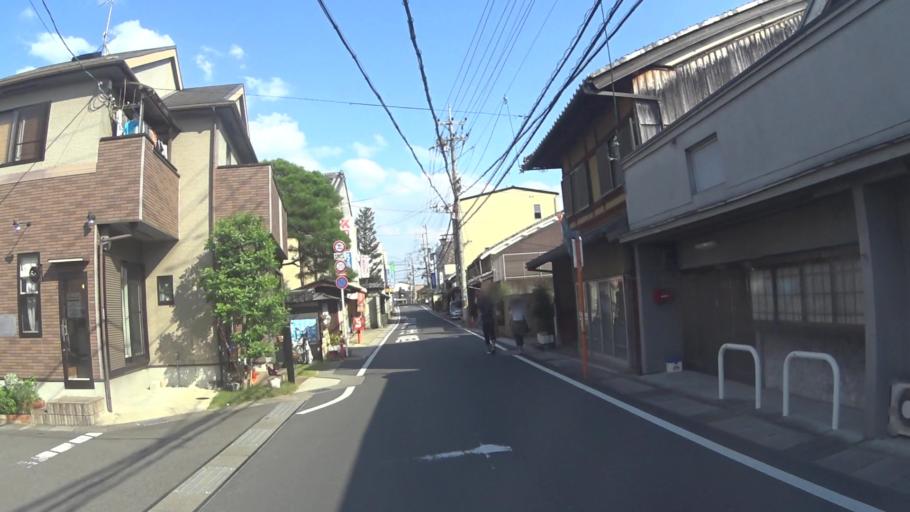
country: JP
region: Kyoto
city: Kameoka
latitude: 35.0186
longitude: 135.5723
